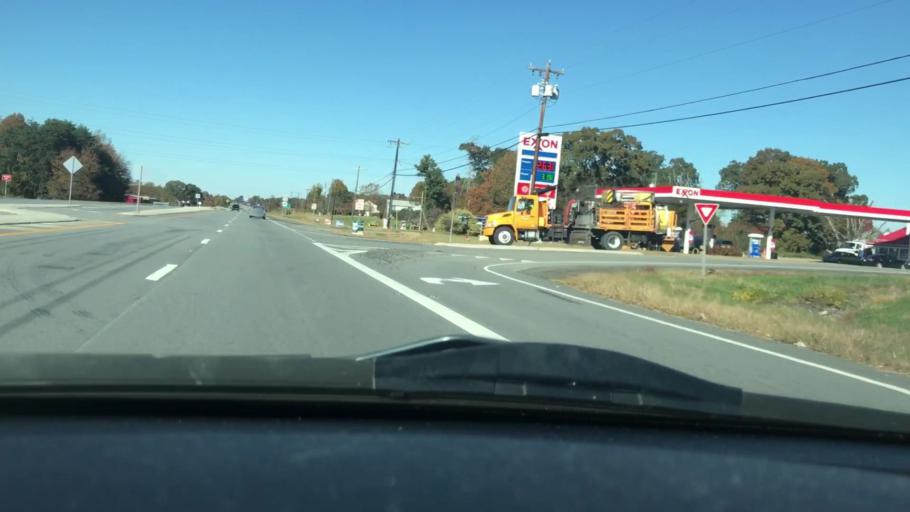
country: US
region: North Carolina
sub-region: Guilford County
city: Stokesdale
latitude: 36.2941
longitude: -79.9401
